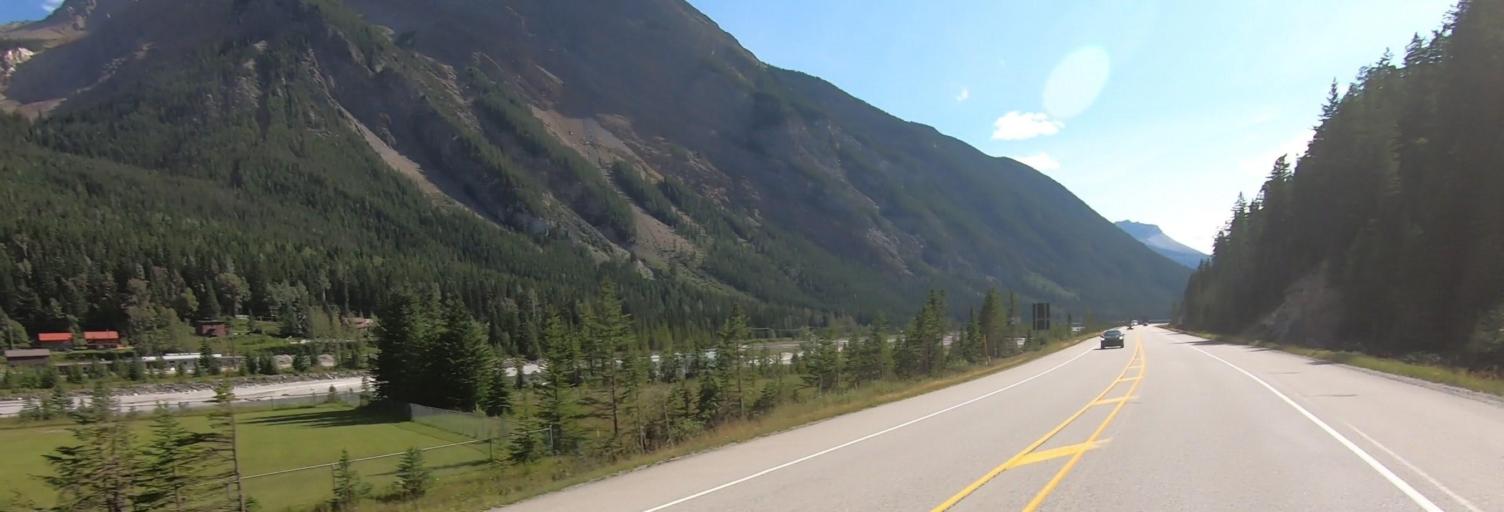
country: CA
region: Alberta
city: Lake Louise
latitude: 51.3961
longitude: -116.4957
